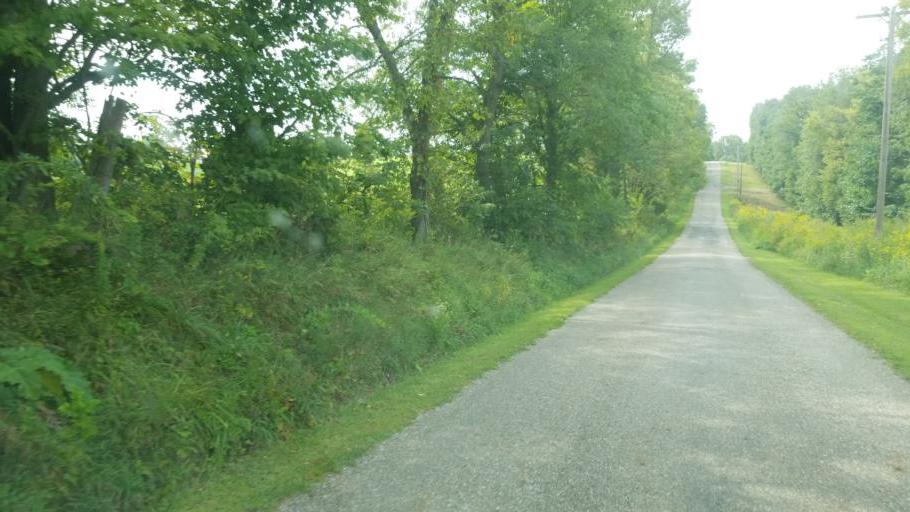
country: US
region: Ohio
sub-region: Knox County
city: Danville
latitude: 40.4909
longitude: -82.3346
